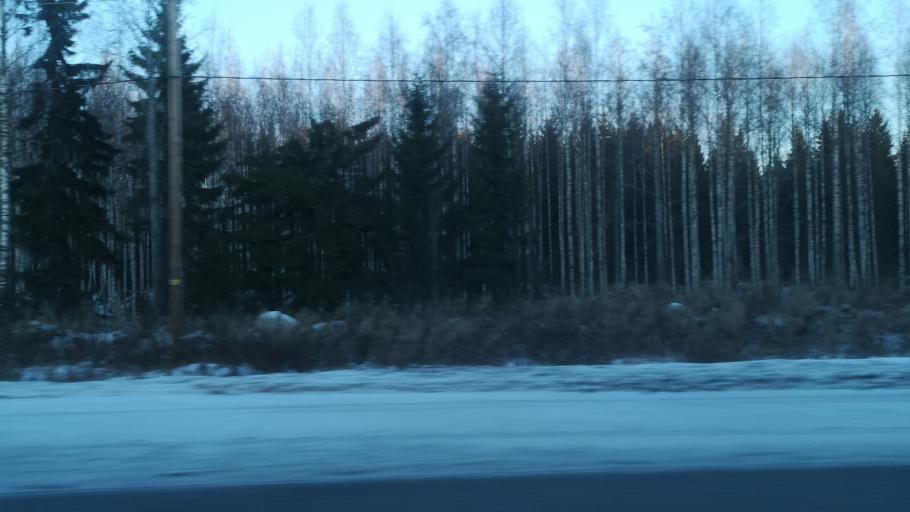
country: FI
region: Southern Savonia
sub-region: Savonlinna
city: Rantasalmi
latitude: 61.9587
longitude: 28.3472
